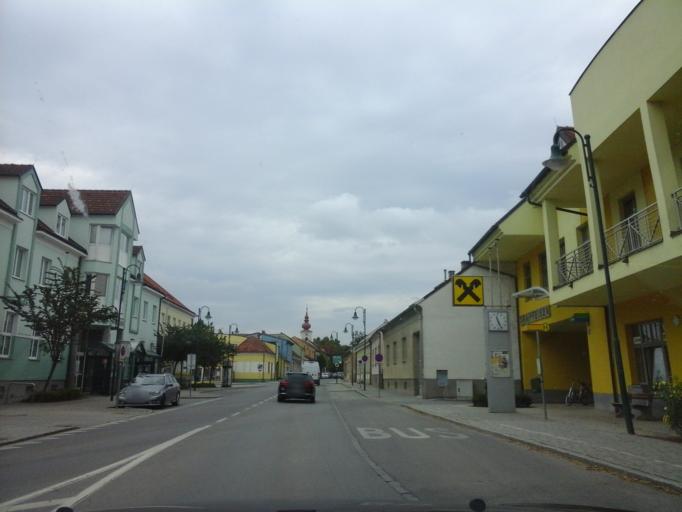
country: AT
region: Lower Austria
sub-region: Politischer Bezirk Ganserndorf
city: Orth an der Donau
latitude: 48.1463
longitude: 16.7033
